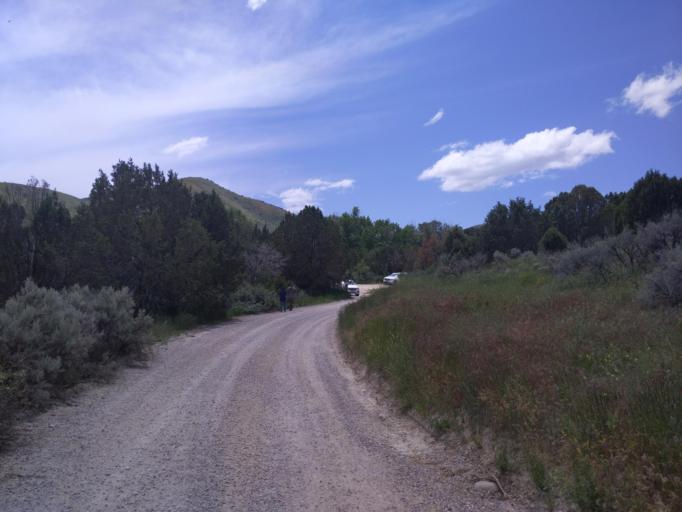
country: US
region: Idaho
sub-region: Bannock County
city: Pocatello
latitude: 42.8416
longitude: -112.4616
